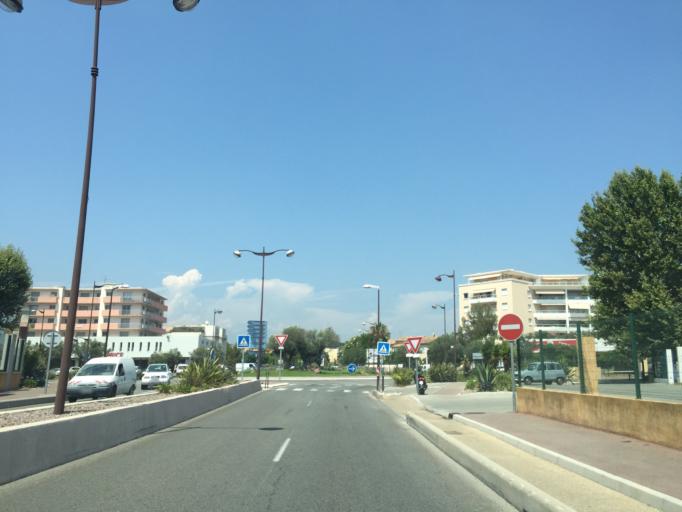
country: FR
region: Provence-Alpes-Cote d'Azur
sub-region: Departement du Var
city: Frejus
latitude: 43.4317
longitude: 6.7495
